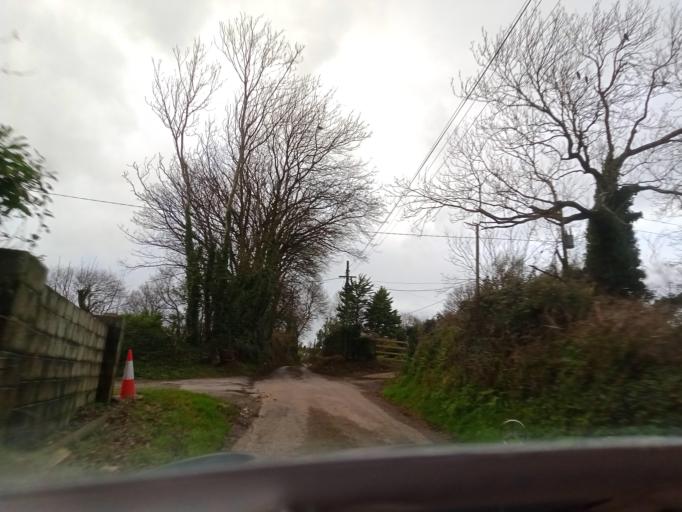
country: IE
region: Munster
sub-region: Waterford
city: Waterford
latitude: 52.3081
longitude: -7.0462
